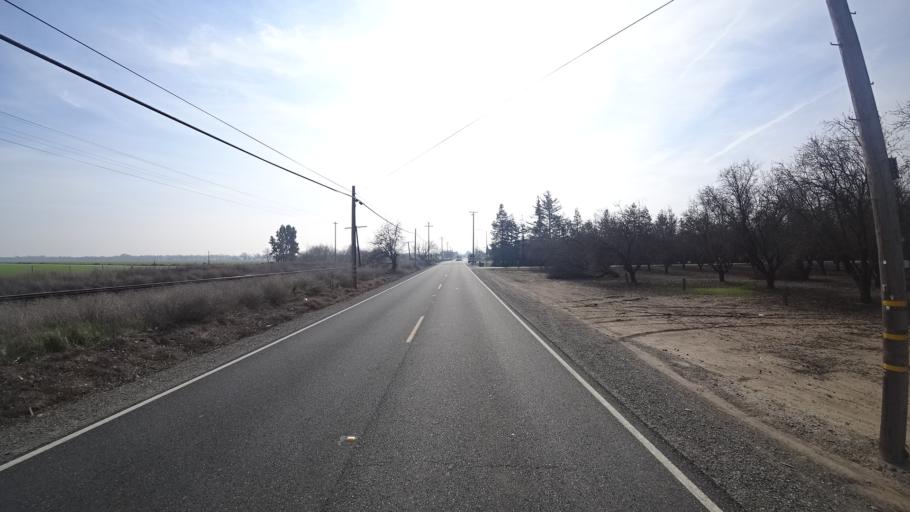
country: US
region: California
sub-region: Yolo County
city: Davis
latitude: 38.5763
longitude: -121.7481
